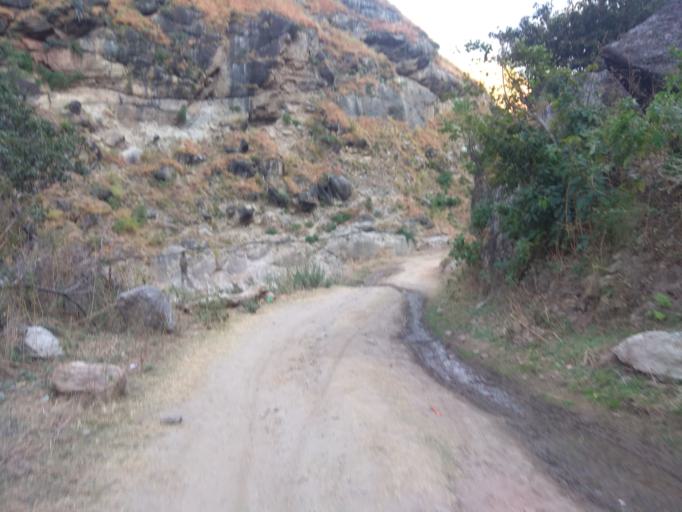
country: NP
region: Far Western
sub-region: Seti Zone
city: Achham
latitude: 29.2276
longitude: 81.6230
